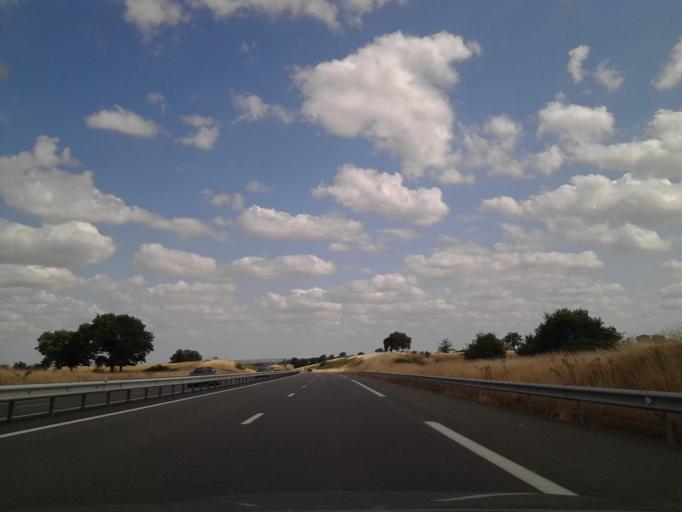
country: FR
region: Auvergne
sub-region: Departement de l'Allier
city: Vallon-en-Sully
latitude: 46.5810
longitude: 2.5259
